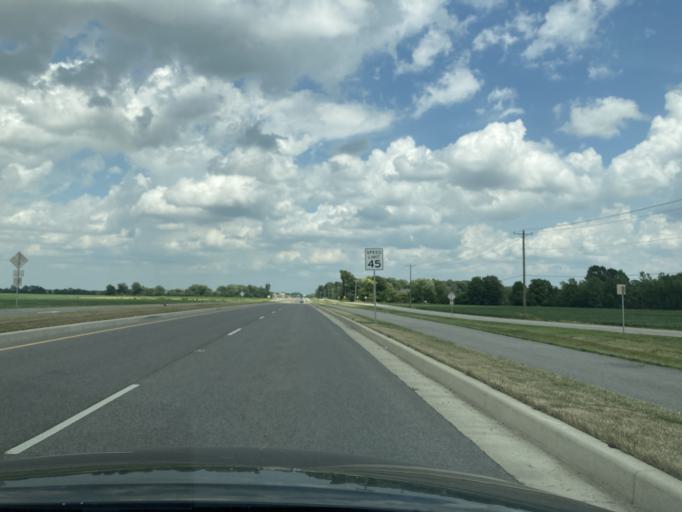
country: US
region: Indiana
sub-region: Boone County
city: Zionsville
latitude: 39.9993
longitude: -86.2018
